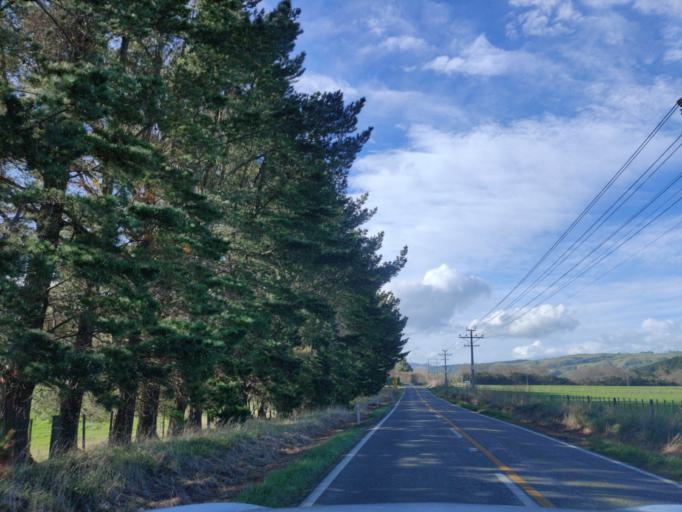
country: NZ
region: Manawatu-Wanganui
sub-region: Palmerston North City
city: Palmerston North
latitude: -40.3374
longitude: 175.7242
